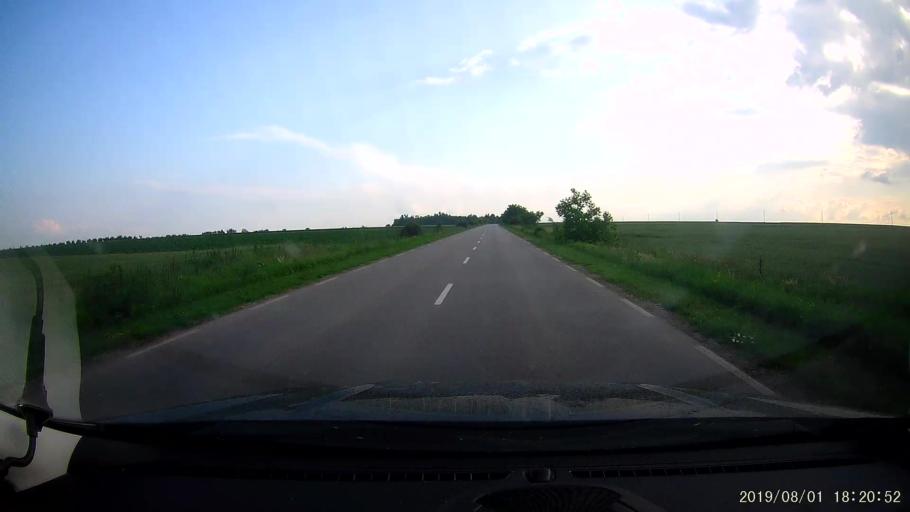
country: BG
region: Shumen
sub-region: Obshtina Kaolinovo
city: Kaolinovo
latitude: 43.6626
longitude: 27.0820
